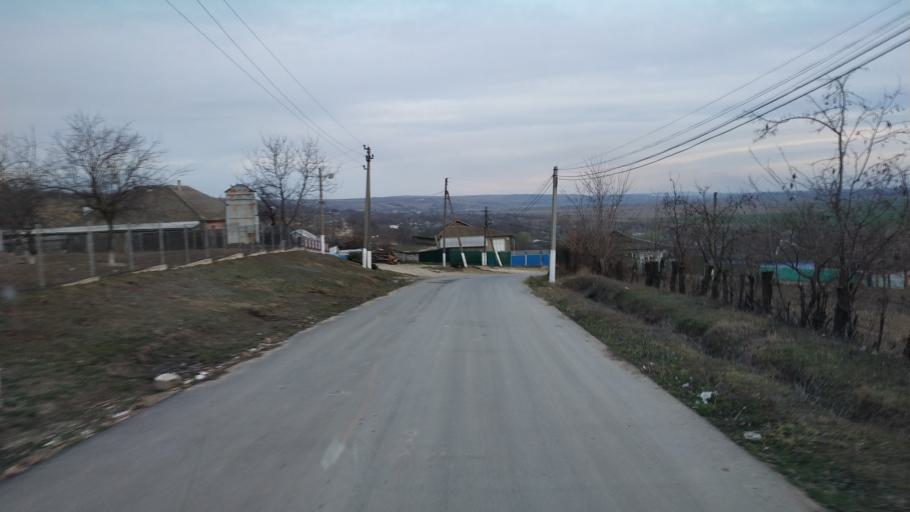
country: MD
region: Hincesti
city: Dancu
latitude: 46.7451
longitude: 28.2103
